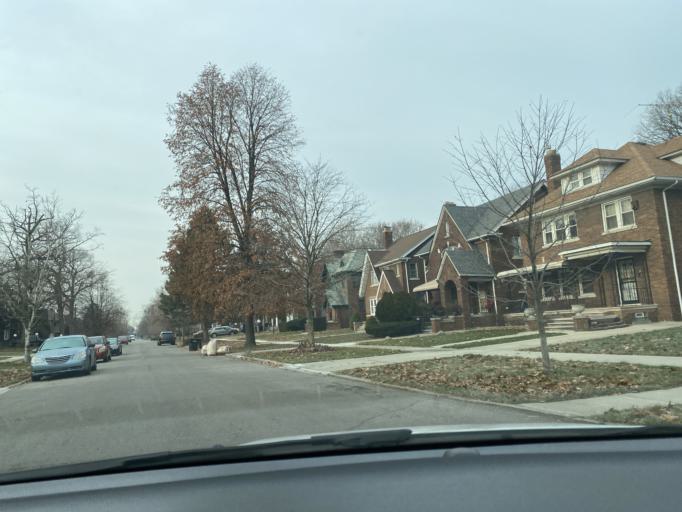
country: US
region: Michigan
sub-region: Wayne County
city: Highland Park
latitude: 42.3843
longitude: -83.1330
